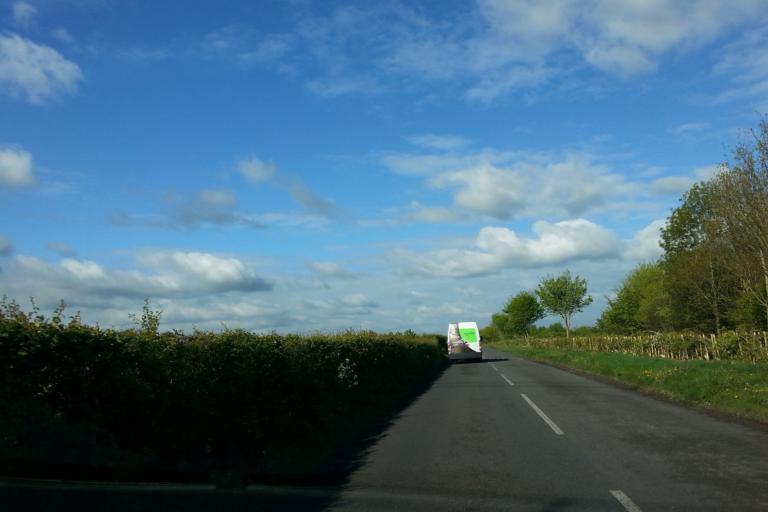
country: GB
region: England
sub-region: Nottinghamshire
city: Cotgrave
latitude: 52.9199
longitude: -1.0204
